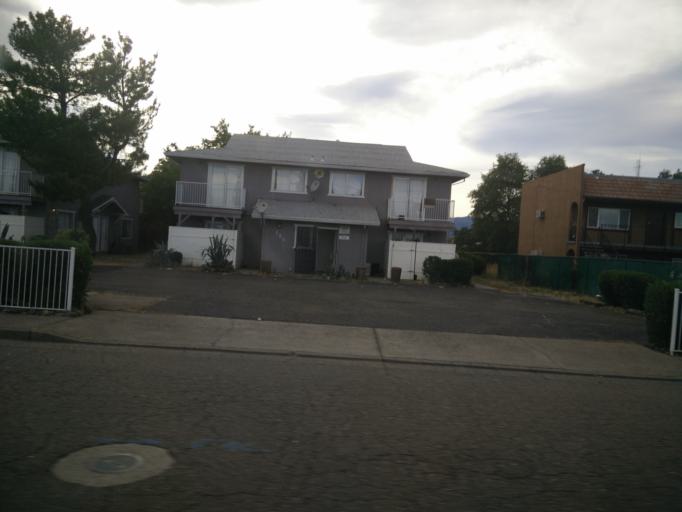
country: US
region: California
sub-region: Shasta County
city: Redding
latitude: 40.6084
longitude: -122.3809
